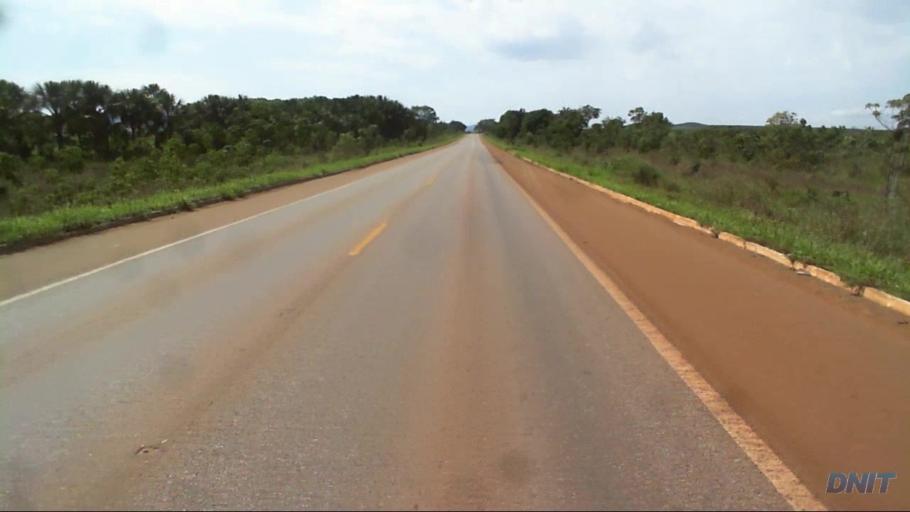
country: BR
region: Goias
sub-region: Barro Alto
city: Barro Alto
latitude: -15.0430
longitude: -48.8893
